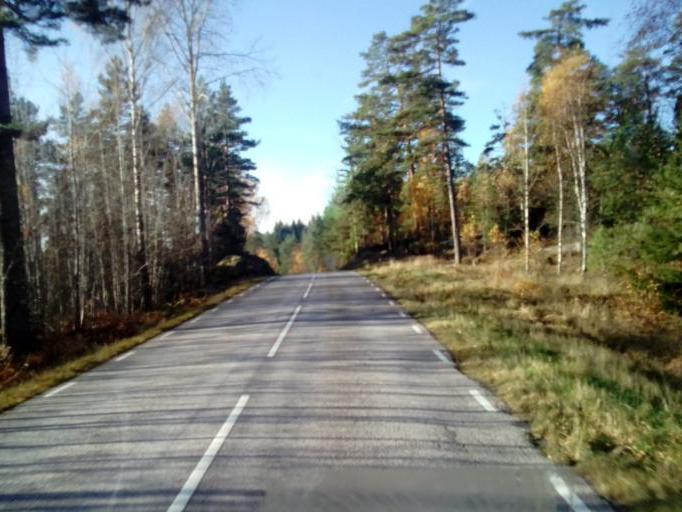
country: SE
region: Kalmar
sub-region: Vasterviks Kommun
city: Ankarsrum
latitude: 57.7714
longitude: 16.1454
